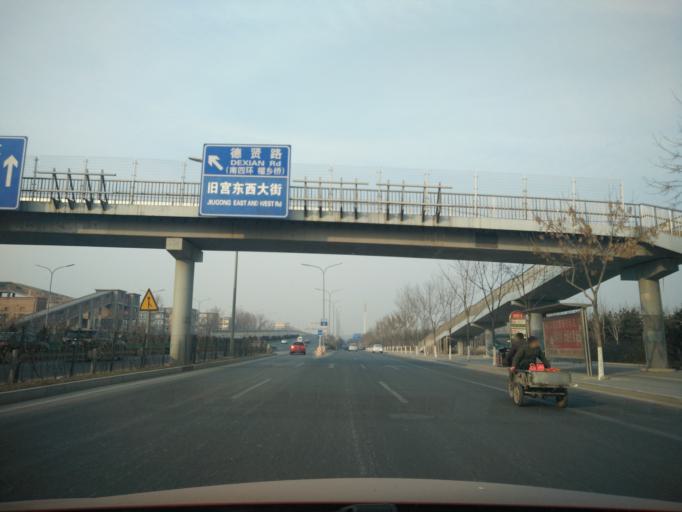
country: CN
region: Beijing
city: Jiugong
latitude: 39.7937
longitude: 116.4239
